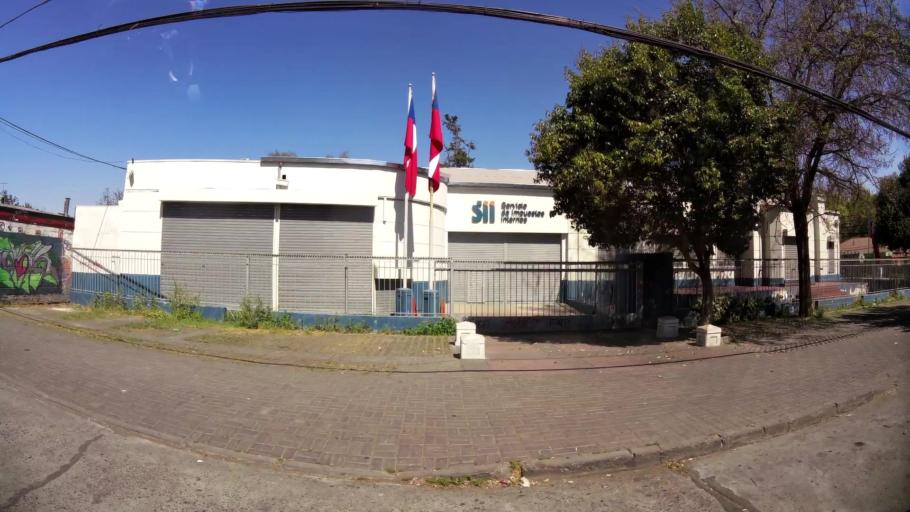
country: CL
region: Santiago Metropolitan
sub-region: Provincia de Santiago
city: Lo Prado
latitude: -33.5189
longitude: -70.7569
